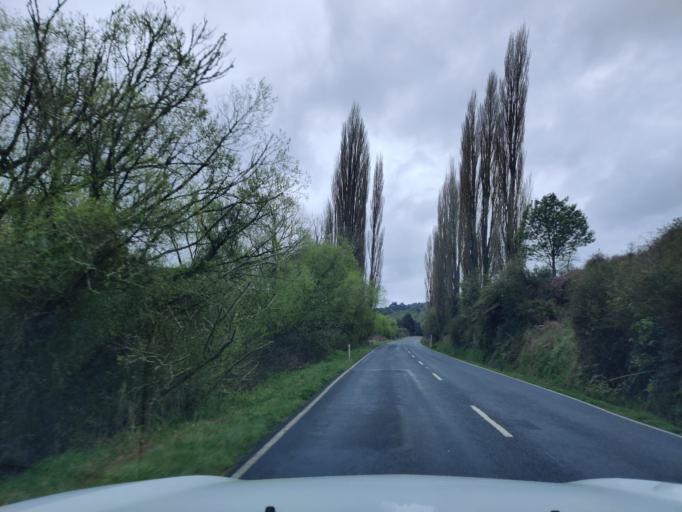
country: NZ
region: Waikato
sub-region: Otorohanga District
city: Otorohanga
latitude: -38.5617
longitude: 175.1972
